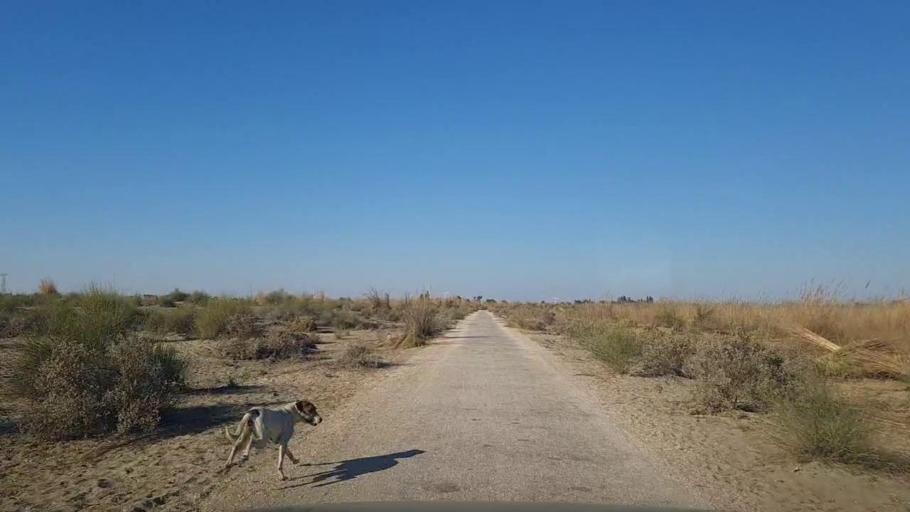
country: PK
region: Sindh
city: Khadro
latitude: 26.2474
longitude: 68.8643
